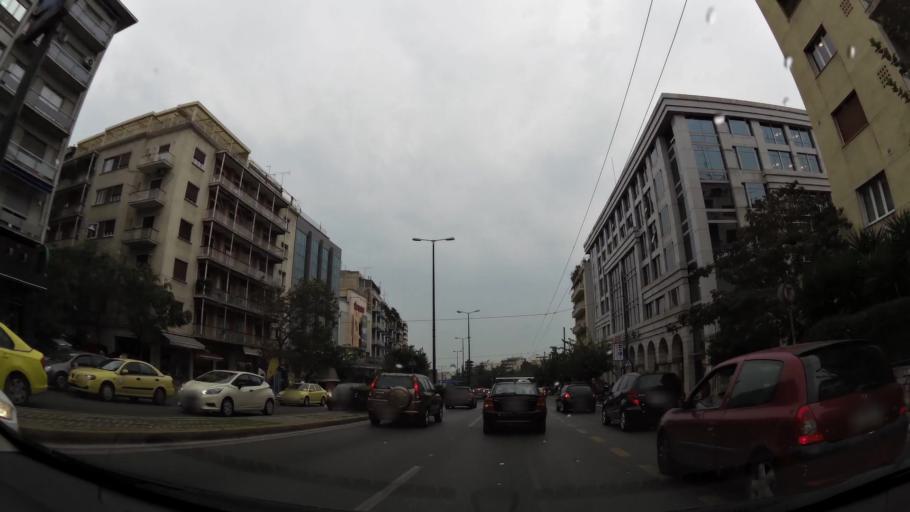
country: GR
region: Attica
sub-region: Nomarchia Athinas
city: Kaisariani
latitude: 37.9876
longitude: 23.7625
